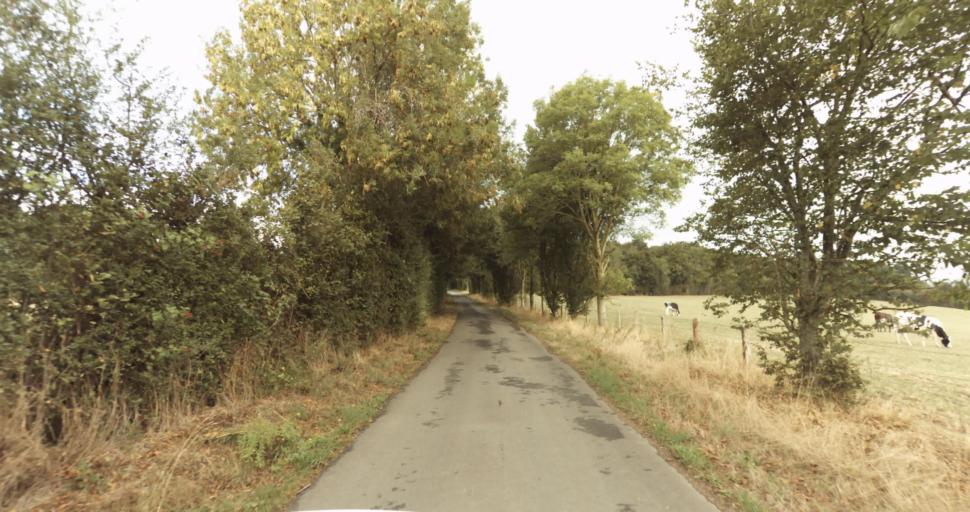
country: FR
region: Lower Normandy
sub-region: Departement de l'Orne
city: Vimoutiers
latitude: 48.9308
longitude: 0.1477
